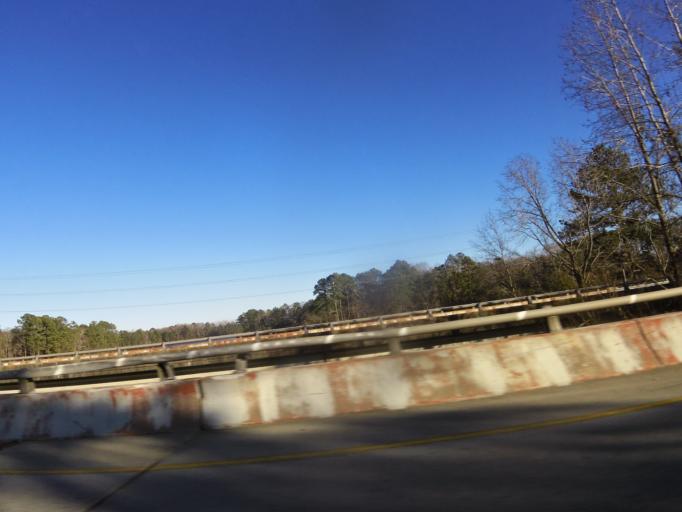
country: US
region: Virginia
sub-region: City of Suffolk
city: Suffolk
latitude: 36.7554
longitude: -76.6105
